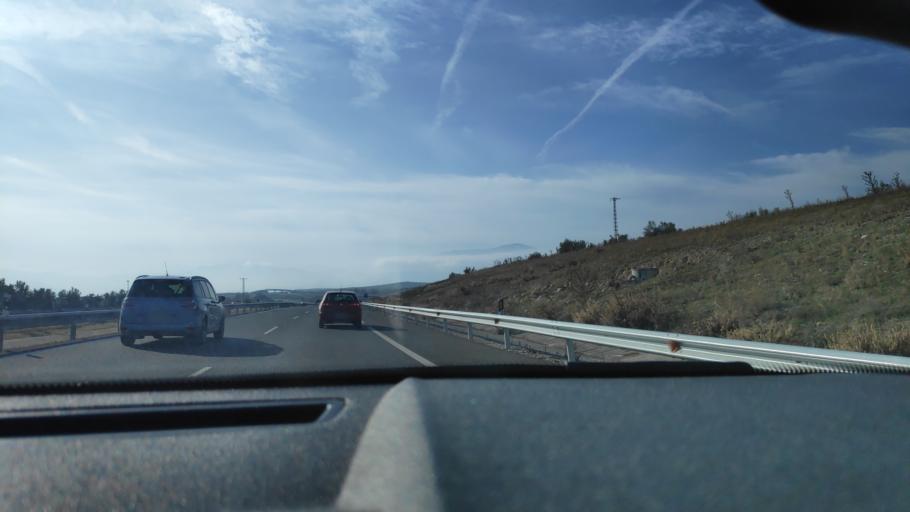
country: ES
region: Andalusia
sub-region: Provincia de Jaen
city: Jaen
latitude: 37.8619
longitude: -3.7640
